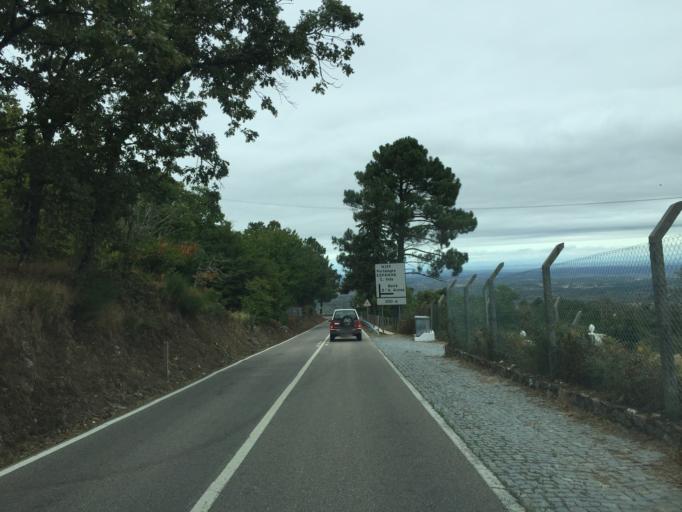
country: PT
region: Portalegre
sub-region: Marvao
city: Marvao
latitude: 39.4018
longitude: -7.3811
